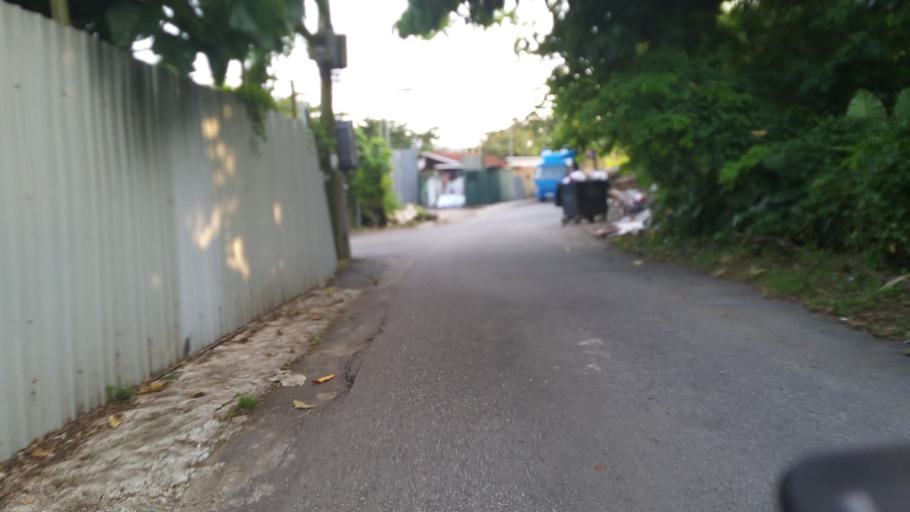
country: HK
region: Yuen Long
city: Yuen Long Kau Hui
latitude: 22.4479
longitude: 114.0147
